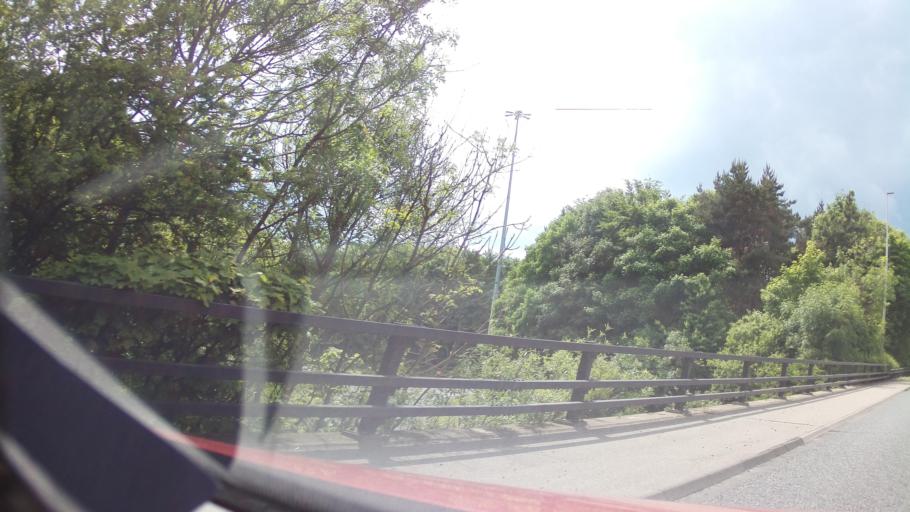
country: GB
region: England
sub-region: Sunderland
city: Washington
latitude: 54.9054
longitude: -1.5120
